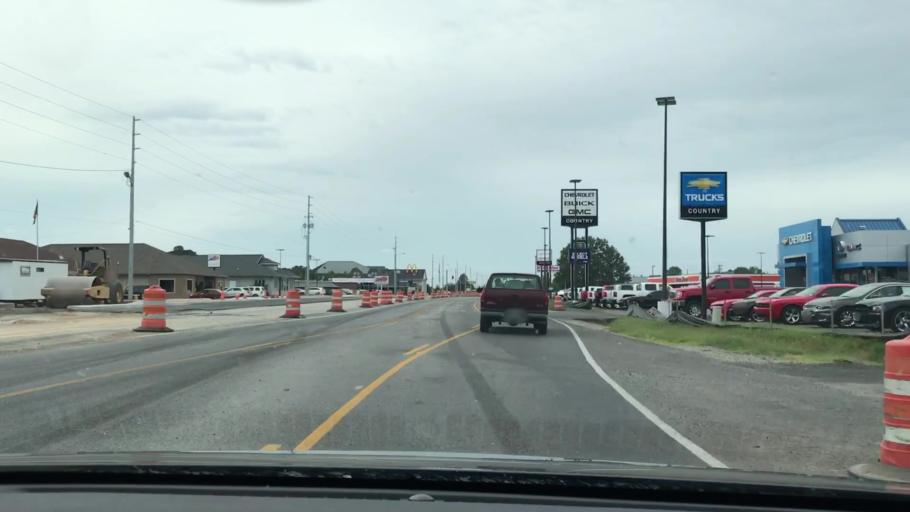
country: US
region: Kentucky
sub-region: Marshall County
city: Benton
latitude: 36.8646
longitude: -88.3527
